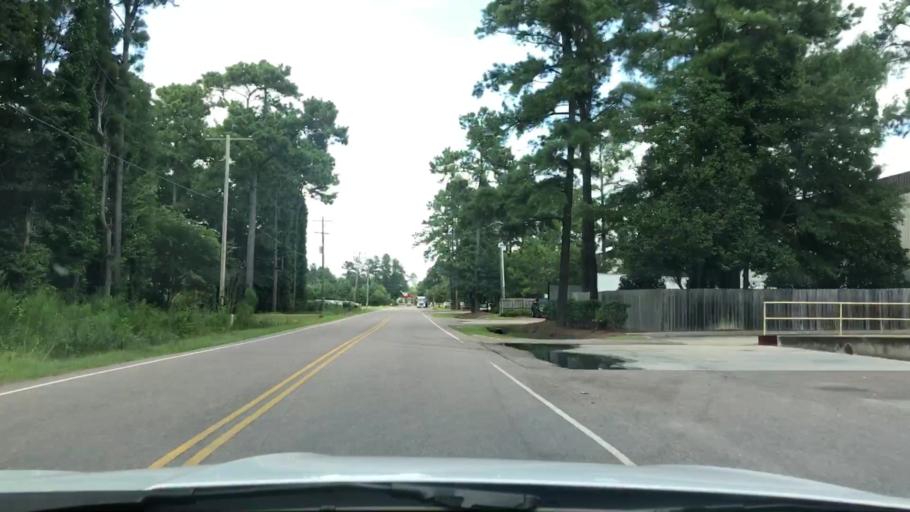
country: US
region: South Carolina
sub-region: Dorchester County
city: Summerville
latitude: 33.0332
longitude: -80.2083
